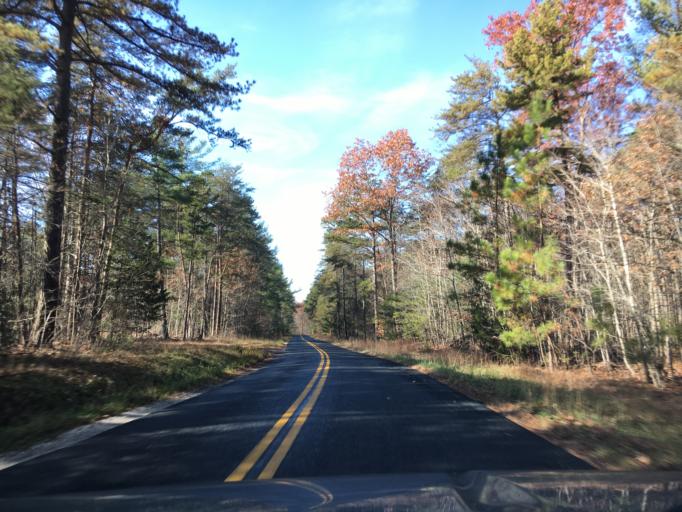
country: US
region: Virginia
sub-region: Buckingham County
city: Buckingham
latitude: 37.4362
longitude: -78.6582
